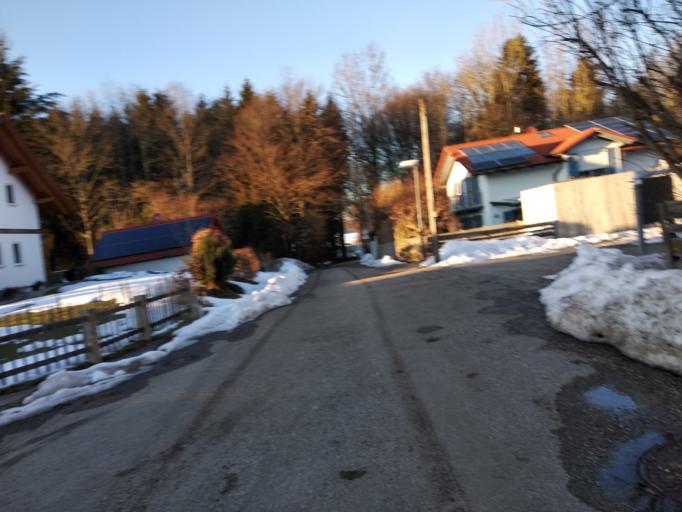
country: DE
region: Bavaria
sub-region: Upper Bavaria
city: Grafing bei Munchen
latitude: 48.0440
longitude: 11.9512
